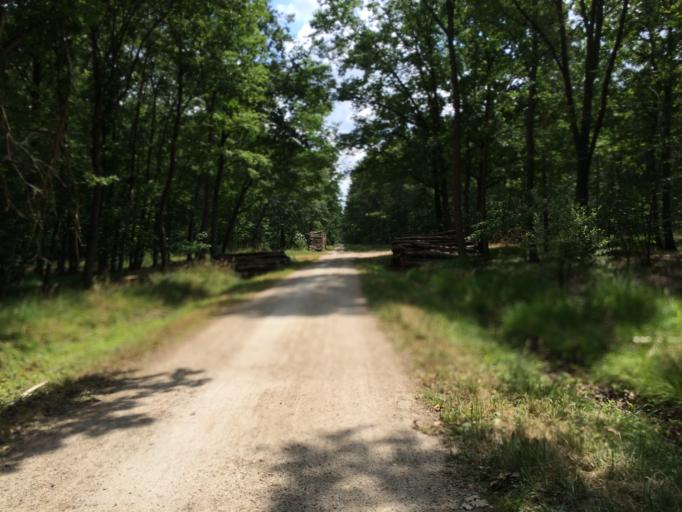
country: FR
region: Ile-de-France
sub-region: Departement de l'Essonne
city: Epinay-sous-Senart
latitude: 48.6669
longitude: 2.5016
